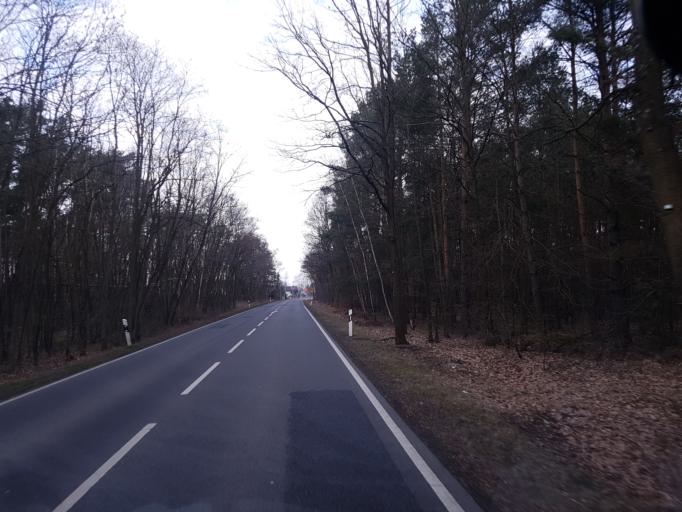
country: DE
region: Brandenburg
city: Finsterwalde
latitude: 51.6108
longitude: 13.7646
